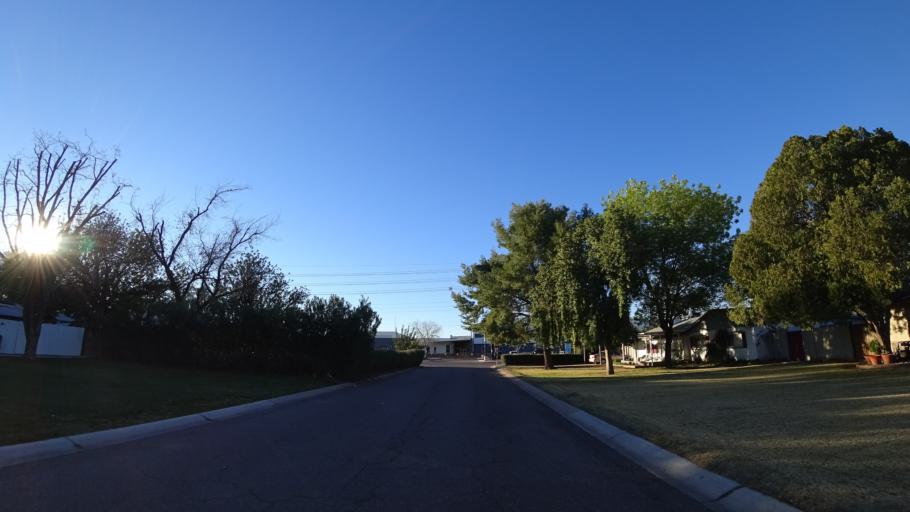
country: US
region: Arizona
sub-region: Maricopa County
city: Paradise Valley
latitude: 33.4884
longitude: -112.0053
